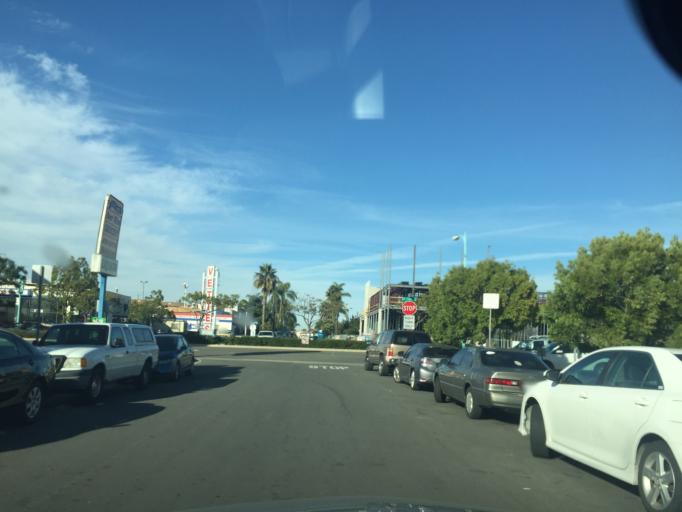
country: US
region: California
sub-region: San Diego County
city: San Diego
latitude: 32.7548
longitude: -117.1211
